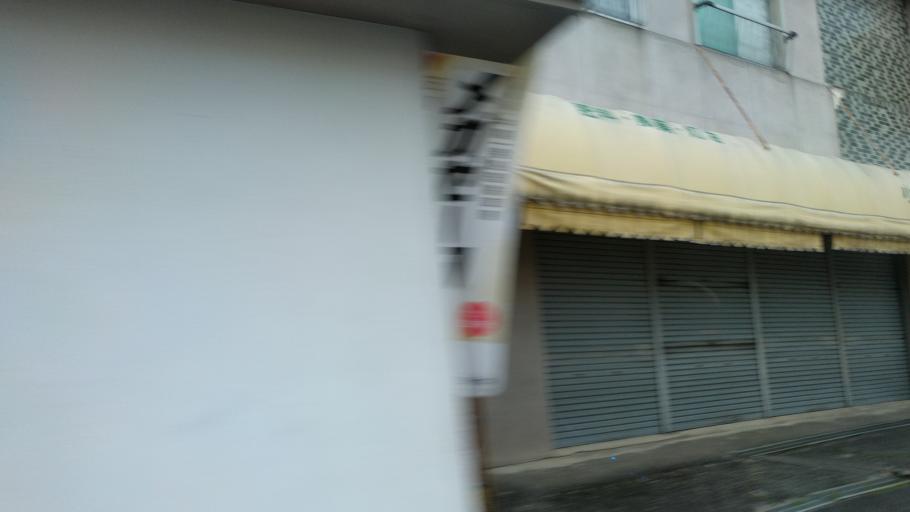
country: JP
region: Fukushima
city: Kitakata
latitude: 37.4468
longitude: 139.8292
